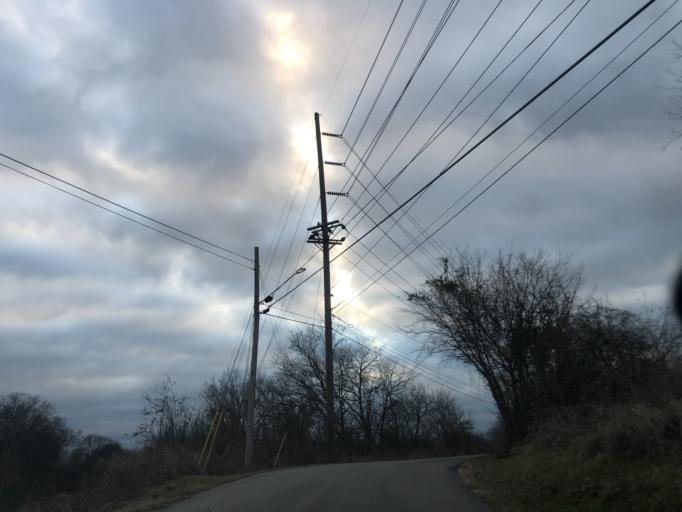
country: US
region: Tennessee
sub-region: Davidson County
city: Goodlettsville
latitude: 36.2876
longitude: -86.6962
